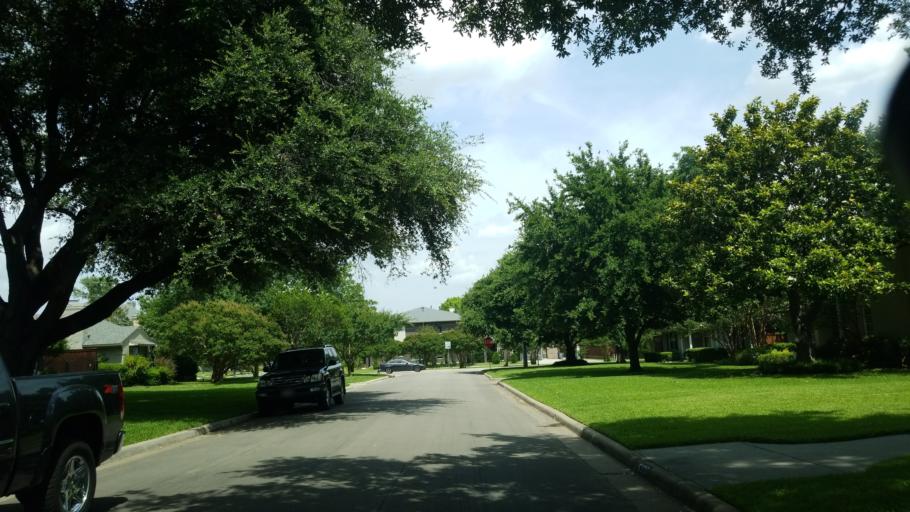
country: US
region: Texas
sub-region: Dallas County
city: University Park
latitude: 32.8685
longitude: -96.7963
